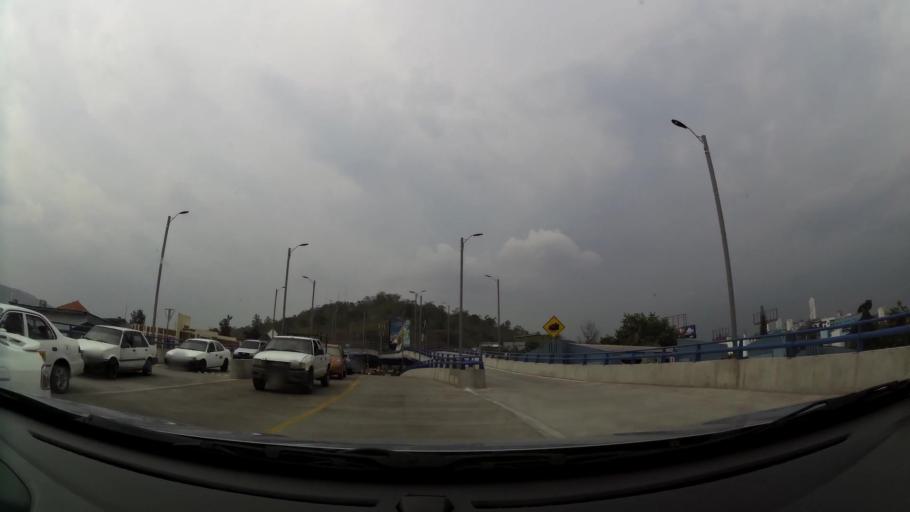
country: HN
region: Francisco Morazan
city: Tegucigalpa
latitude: 14.0873
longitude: -87.2026
